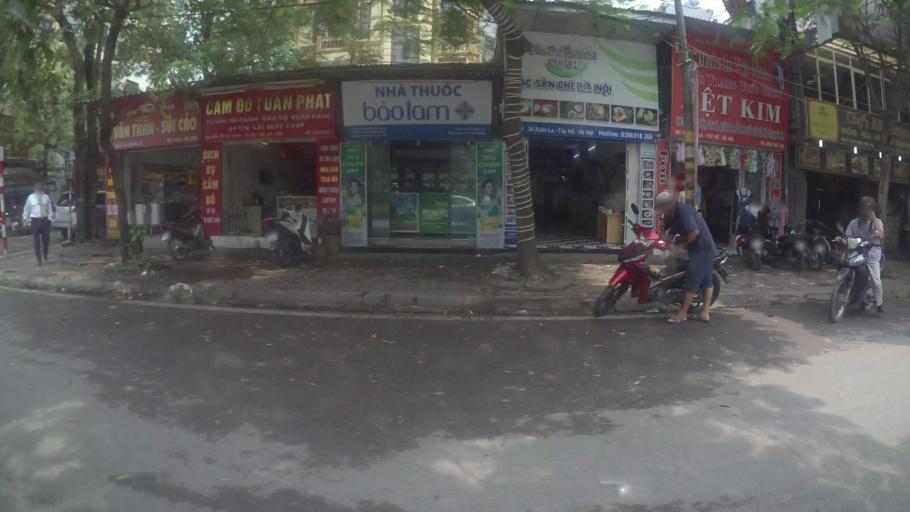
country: VN
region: Ha Noi
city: Tay Ho
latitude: 21.0662
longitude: 105.8048
